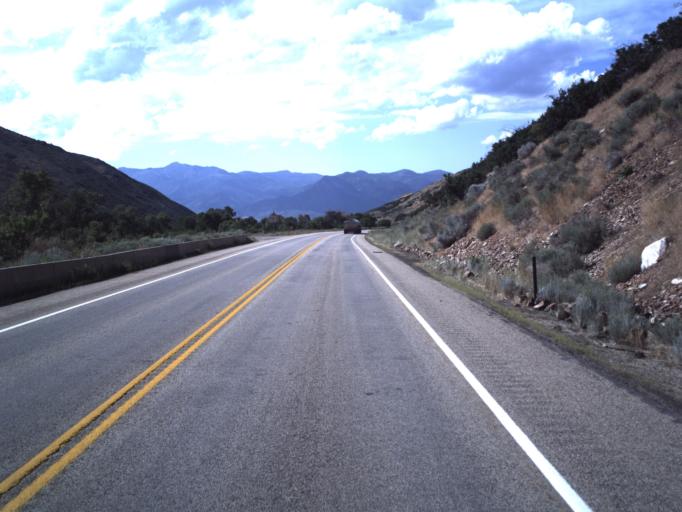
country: US
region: Utah
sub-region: Wasatch County
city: Heber
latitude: 40.4357
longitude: -111.3563
